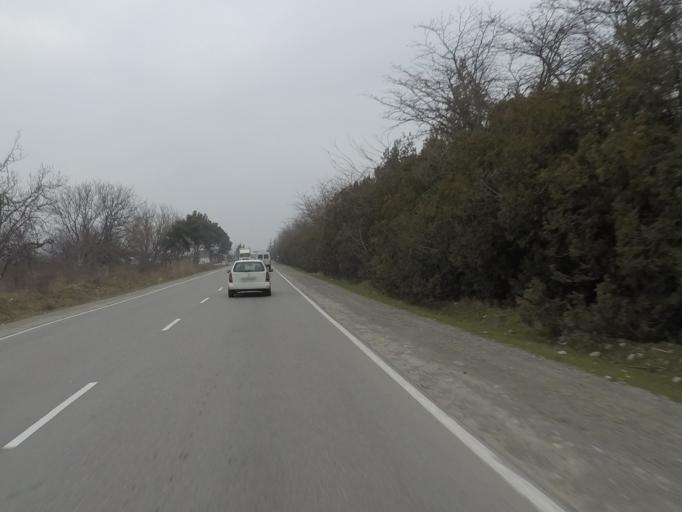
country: GE
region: Mtskheta-Mtianeti
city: Mtskheta
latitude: 41.9069
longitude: 44.7233
